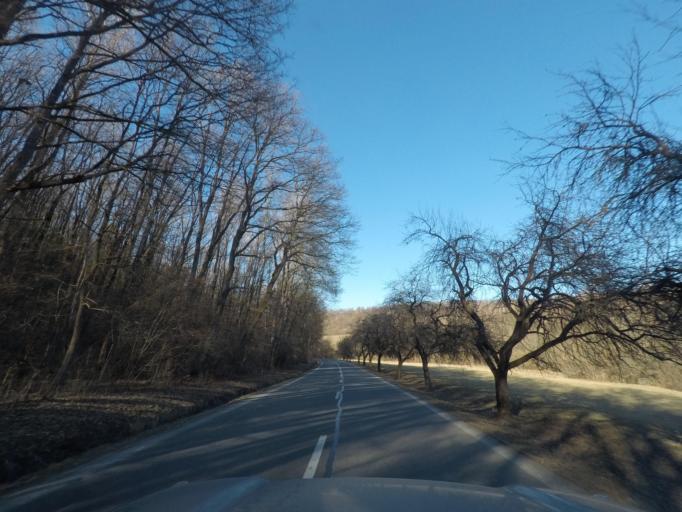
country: SK
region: Presovsky
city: Medzilaborce
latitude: 49.1688
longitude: 22.0229
